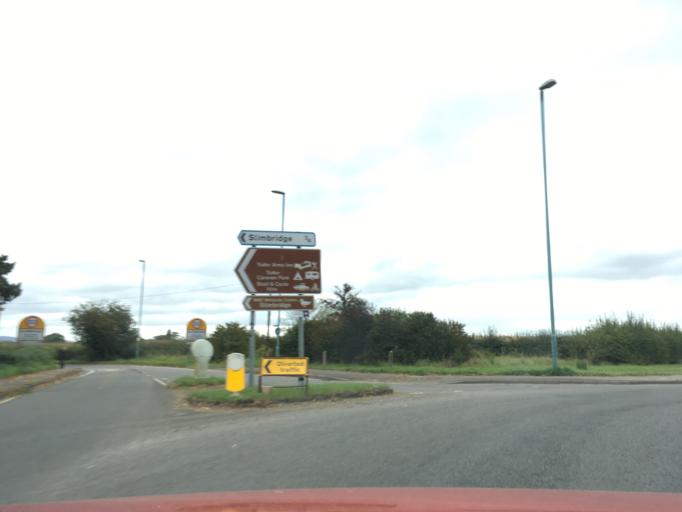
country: GB
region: England
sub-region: Gloucestershire
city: Dursley
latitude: 51.7235
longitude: -2.3725
